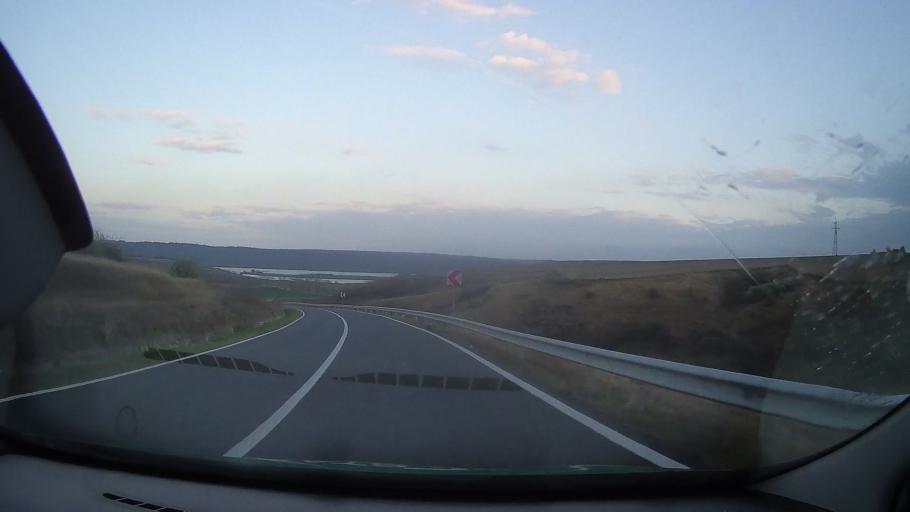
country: RO
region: Constanta
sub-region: Comuna Lipnita
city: Lipnita
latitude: 44.0979
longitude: 27.6221
